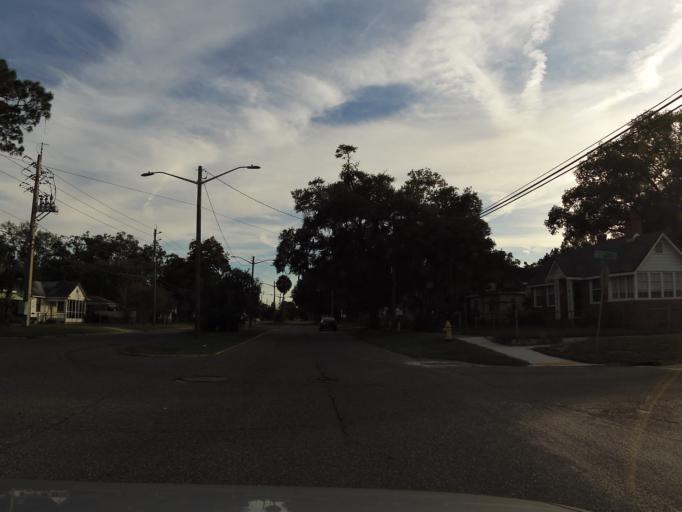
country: US
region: Florida
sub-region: Duval County
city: Jacksonville
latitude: 30.3847
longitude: -81.6568
